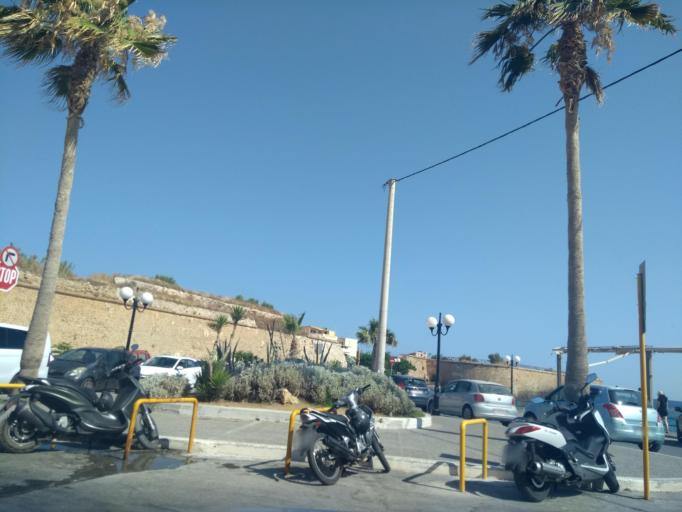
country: GR
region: Crete
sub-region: Nomos Chanias
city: Chania
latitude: 35.5171
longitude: 24.0247
